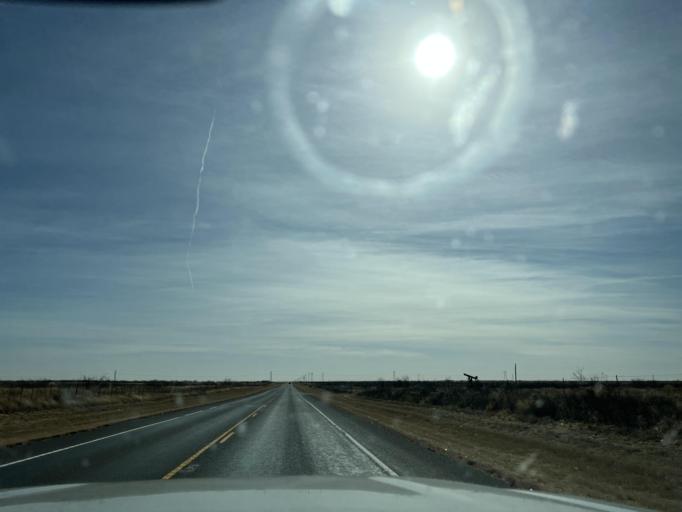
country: US
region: Texas
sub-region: Andrews County
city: Andrews
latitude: 32.4272
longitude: -102.4362
